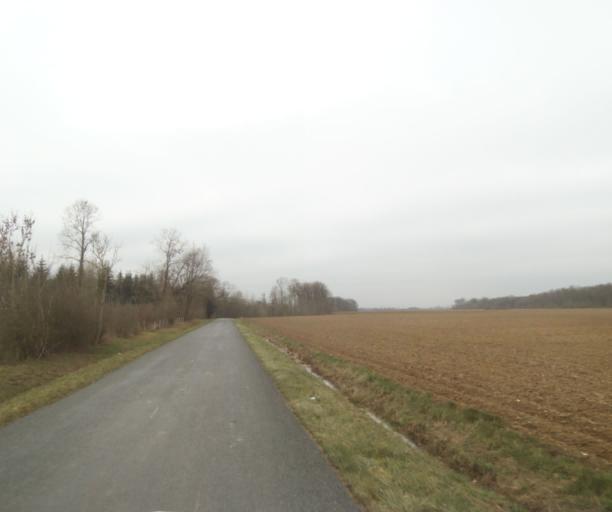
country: FR
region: Champagne-Ardenne
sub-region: Departement de la Marne
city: Pargny-sur-Saulx
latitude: 48.7368
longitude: 4.8227
